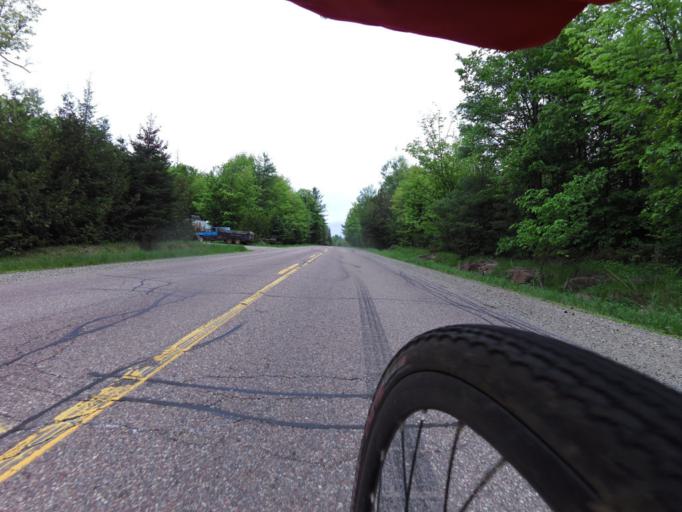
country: CA
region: Ontario
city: Renfrew
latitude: 45.2872
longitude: -76.6846
